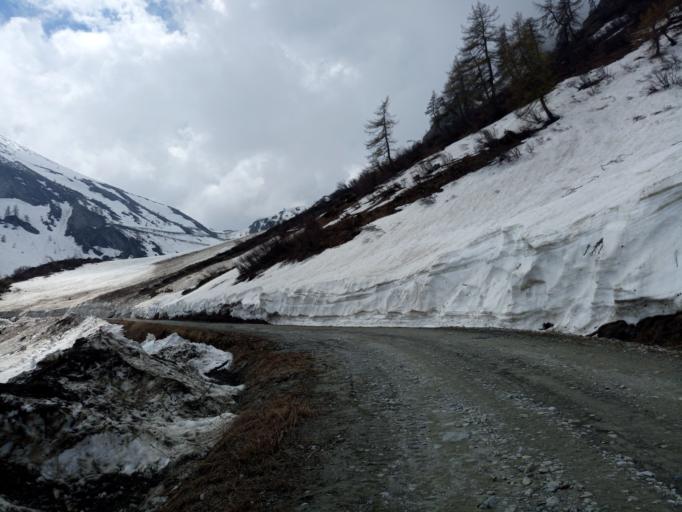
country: IT
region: Piedmont
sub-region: Provincia di Torino
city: Usseaux
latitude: 45.0802
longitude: 7.0539
